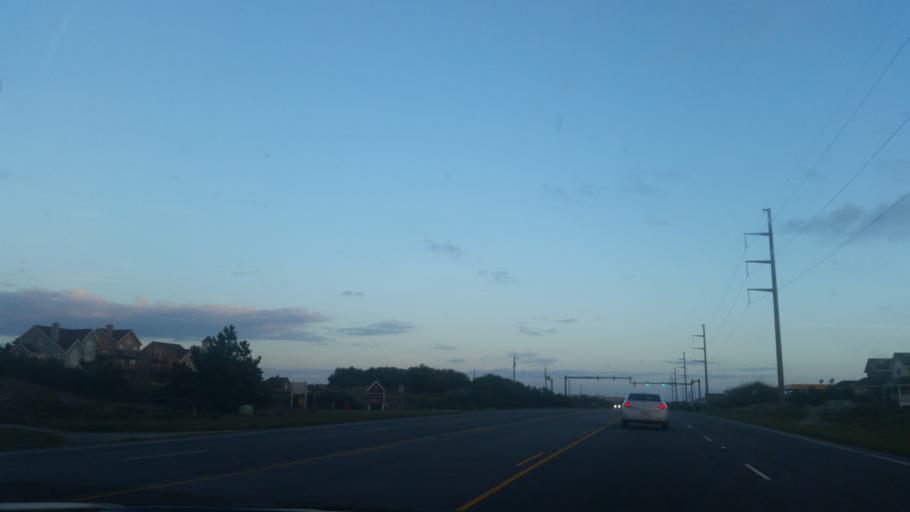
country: US
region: North Carolina
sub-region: Dare County
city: Nags Head
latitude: 35.9497
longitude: -75.6218
